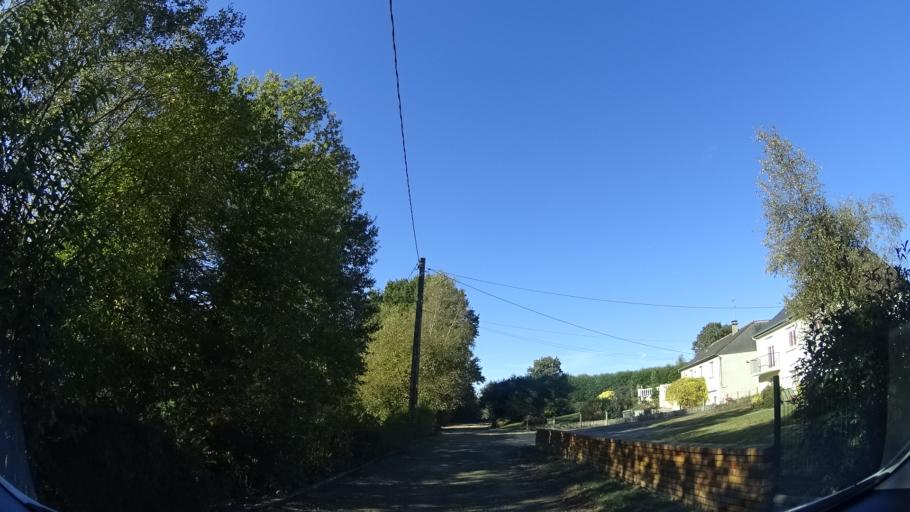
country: FR
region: Brittany
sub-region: Departement d'Ille-et-Vilaine
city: La Meziere
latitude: 48.2146
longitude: -1.7670
